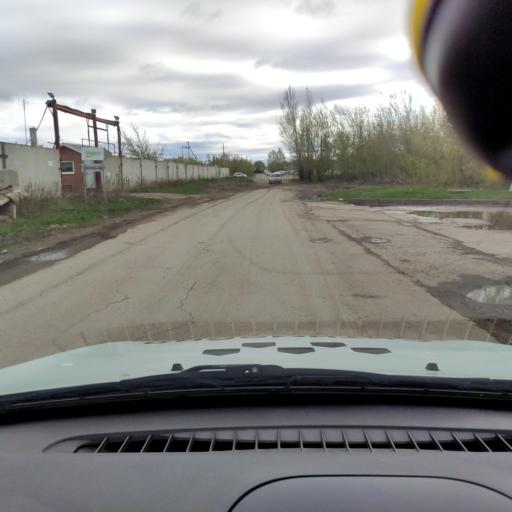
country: RU
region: Samara
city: Tol'yatti
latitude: 53.5800
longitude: 49.3139
